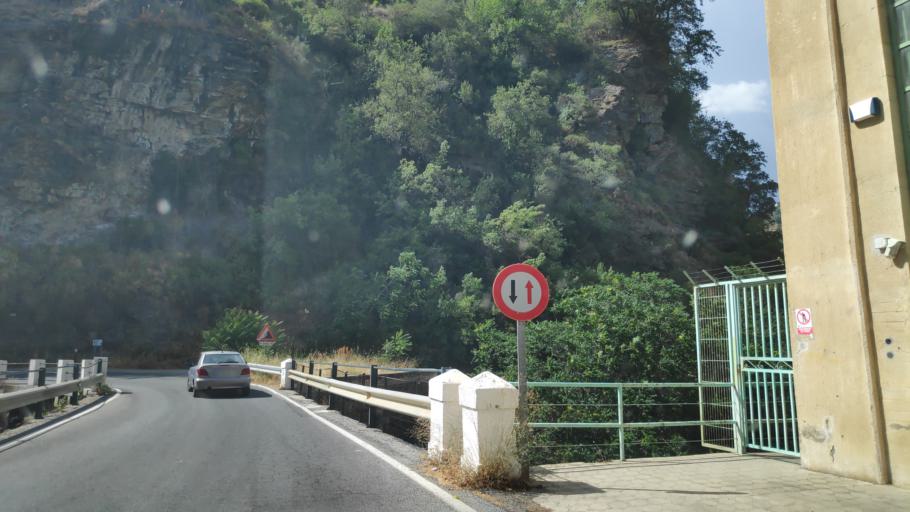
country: ES
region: Andalusia
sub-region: Provincia de Granada
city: Pampaneira
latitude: 36.9423
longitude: -3.3637
